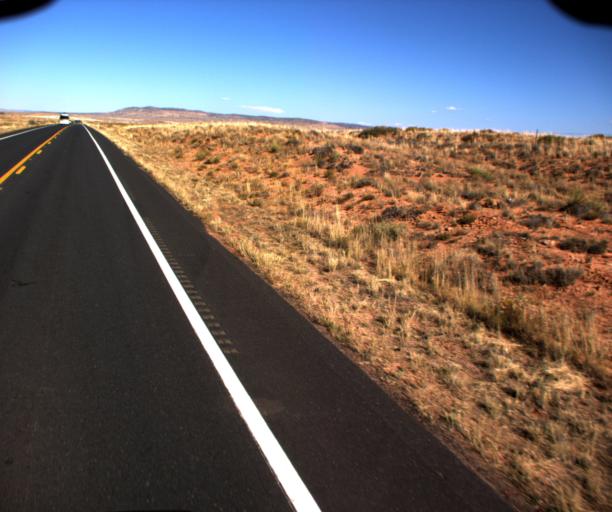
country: US
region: Arizona
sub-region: Coconino County
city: Kaibito
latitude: 36.3071
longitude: -110.9667
